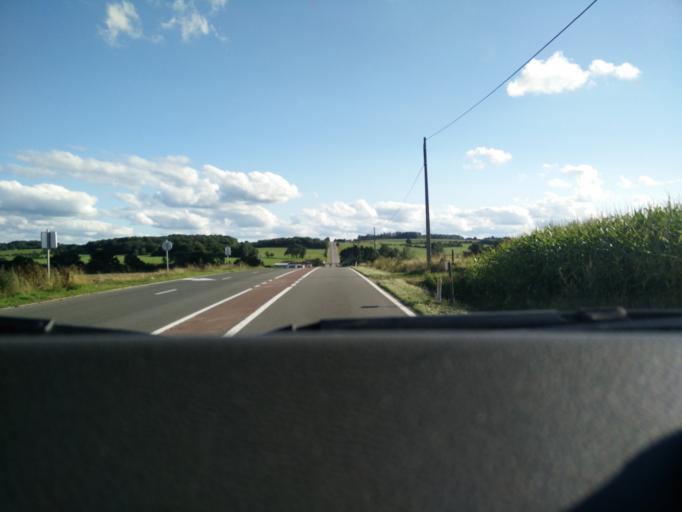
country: BE
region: Wallonia
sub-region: Province du Hainaut
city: Beaumont
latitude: 50.2216
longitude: 4.2277
